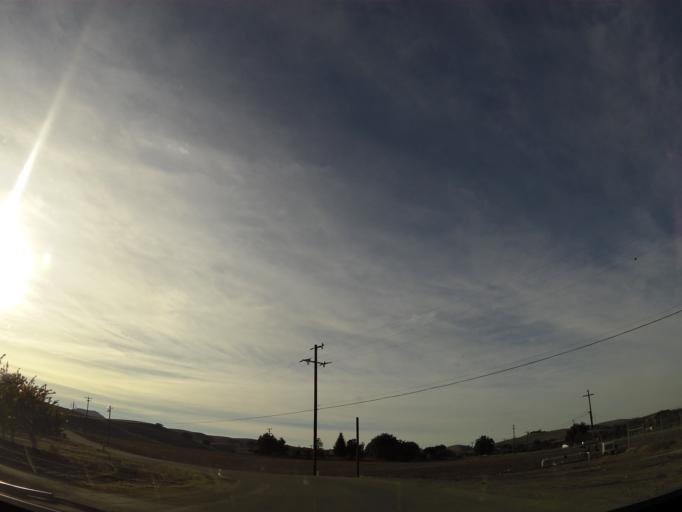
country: US
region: California
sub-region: San Benito County
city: Hollister
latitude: 36.8238
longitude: -121.4067
